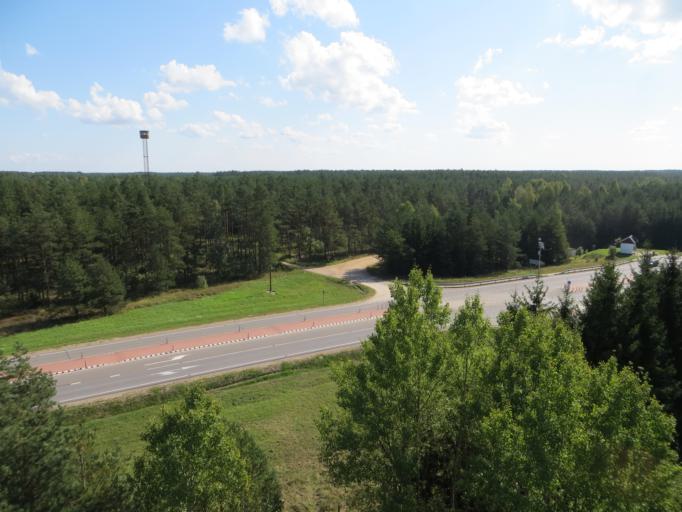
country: LT
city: Trakai
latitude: 54.5030
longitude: 24.9884
